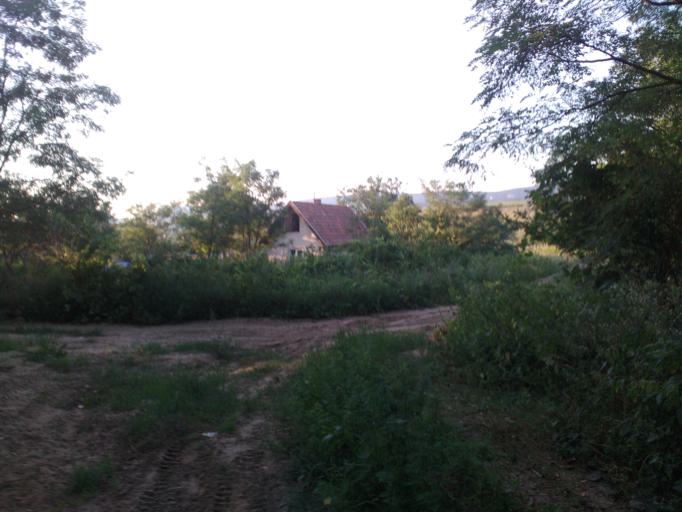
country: HU
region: Komarom-Esztergom
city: Piliscsev
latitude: 47.6703
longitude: 18.8235
